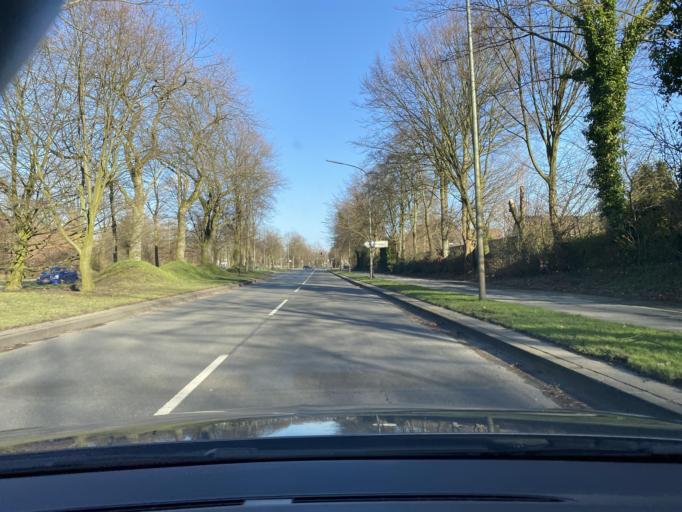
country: DE
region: North Rhine-Westphalia
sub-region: Regierungsbezirk Munster
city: Gelsenkirchen
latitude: 51.5227
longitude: 7.0494
